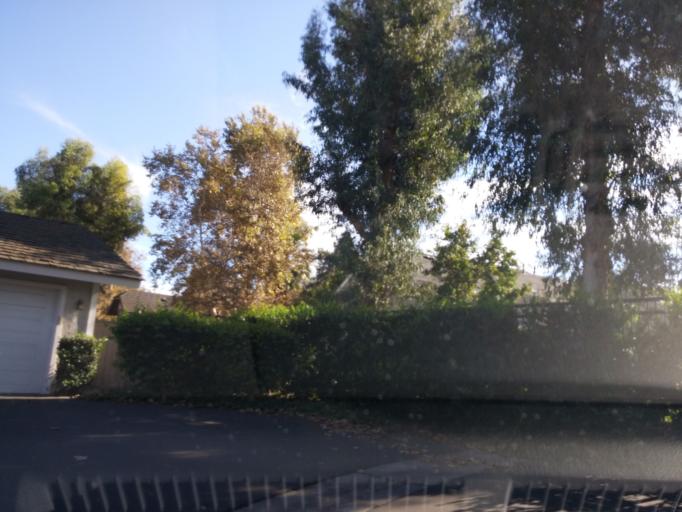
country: US
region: California
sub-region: Orange County
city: Irvine
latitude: 33.6798
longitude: -117.7856
